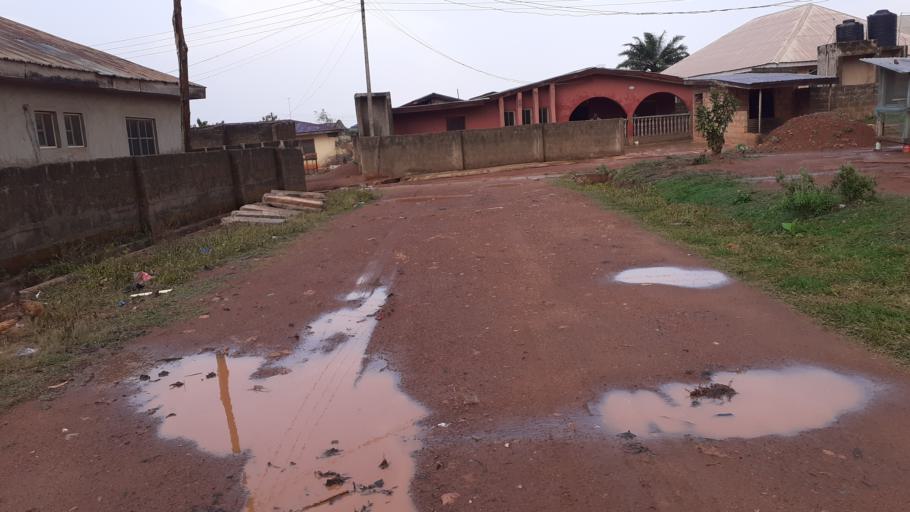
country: NG
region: Ondo
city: Akure
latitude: 7.2150
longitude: 5.2164
